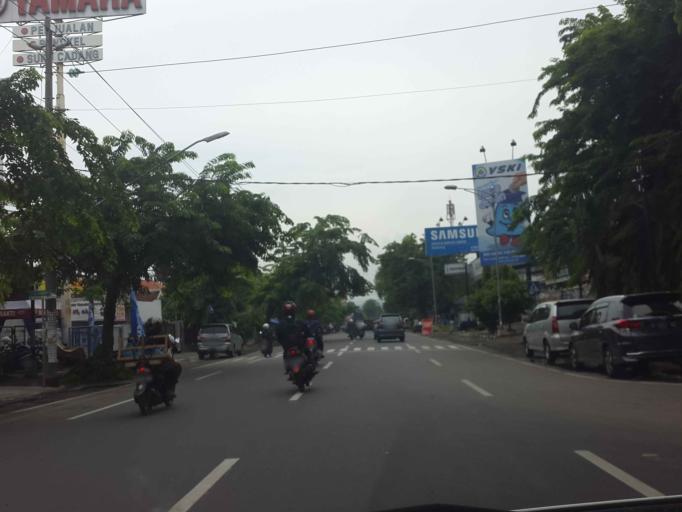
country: ID
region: Central Java
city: Semarang
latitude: -6.9829
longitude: 110.4349
